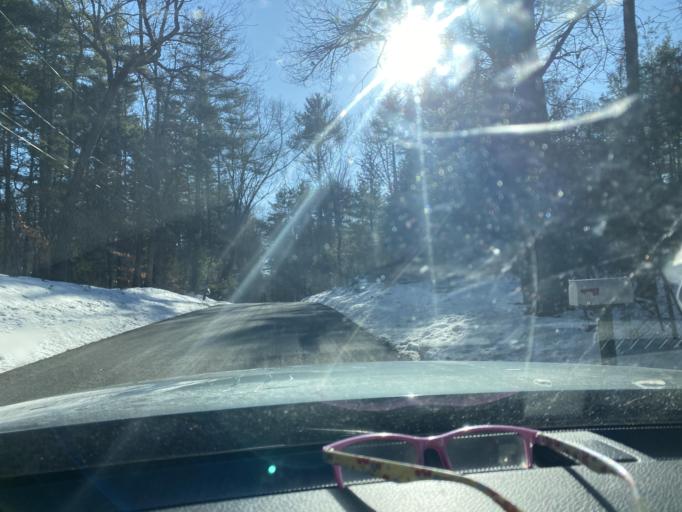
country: US
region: Massachusetts
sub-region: Norfolk County
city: Medfield
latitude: 42.1791
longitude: -71.2806
